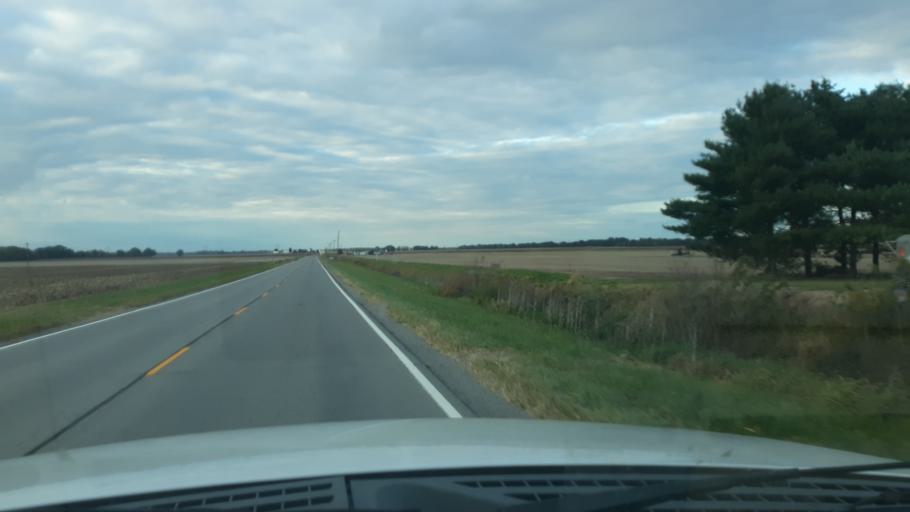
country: US
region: Illinois
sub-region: Saline County
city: Eldorado
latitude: 37.8351
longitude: -88.4528
